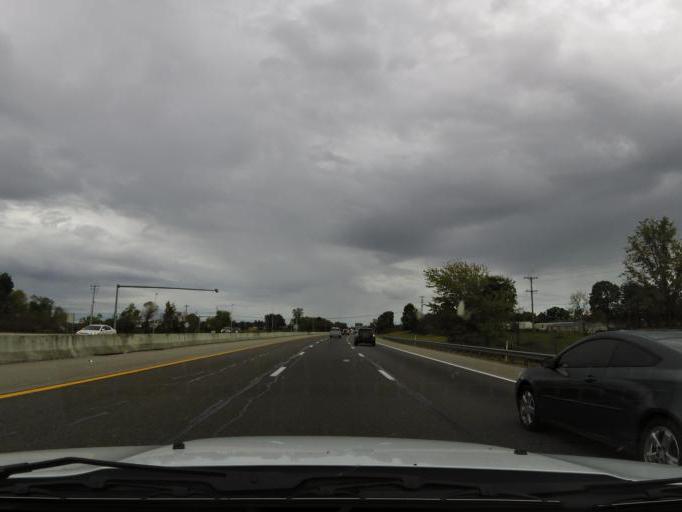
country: US
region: Kentucky
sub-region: Laurel County
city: London
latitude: 37.0477
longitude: -84.0988
